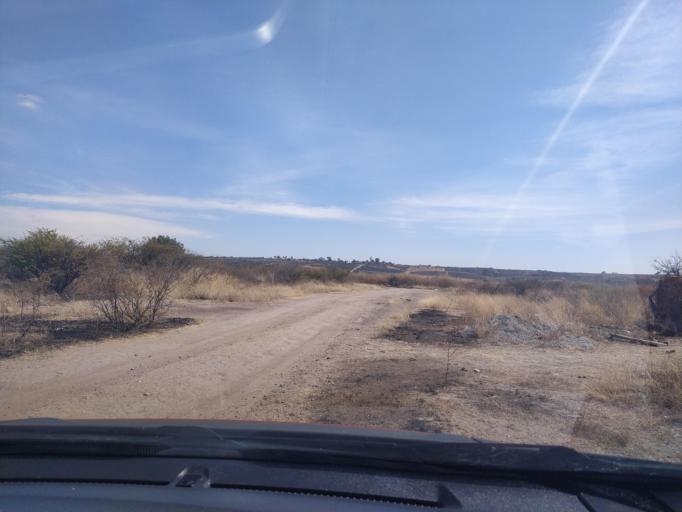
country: MX
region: Guanajuato
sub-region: San Francisco del Rincon
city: San Ignacio de Hidalgo
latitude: 20.8815
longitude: -101.8413
